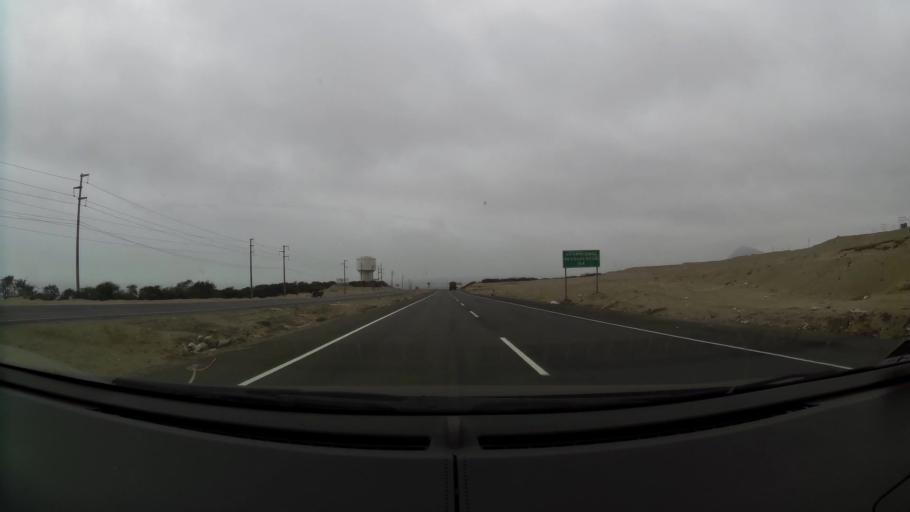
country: PE
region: La Libertad
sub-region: Provincia de Trujillo
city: Salaverry
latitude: -8.1916
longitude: -78.9748
